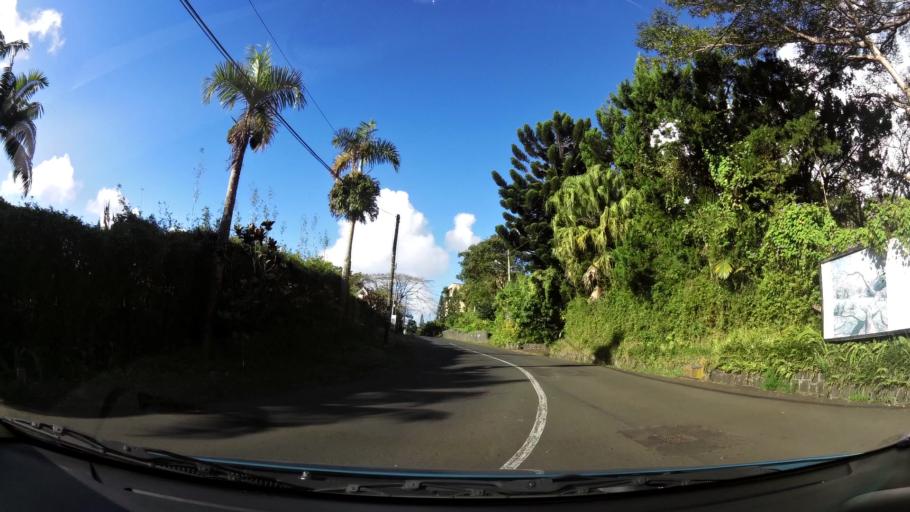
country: MU
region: Plaines Wilhems
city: Curepipe
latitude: -20.3129
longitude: 57.5048
